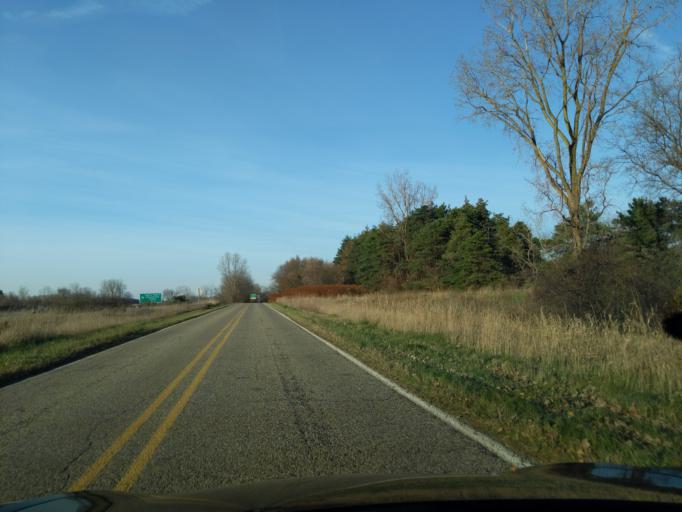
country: US
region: Michigan
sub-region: Ingham County
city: East Lansing
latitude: 42.7881
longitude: -84.5130
